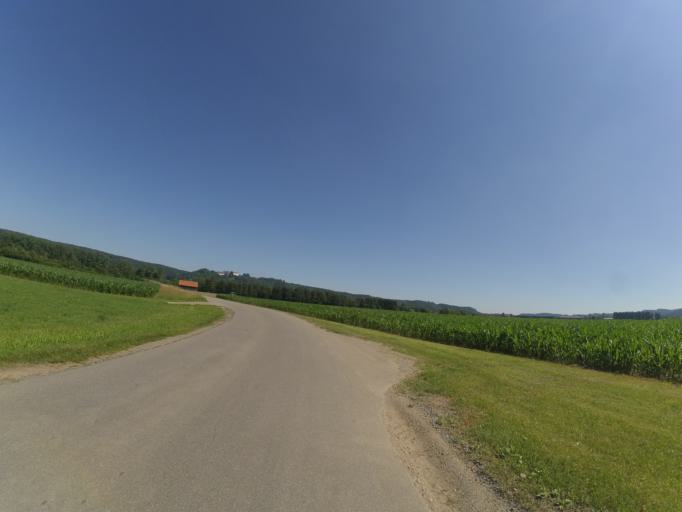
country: DE
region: Baden-Wuerttemberg
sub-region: Tuebingen Region
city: Leutkirch im Allgau
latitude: 47.8490
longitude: 9.9969
